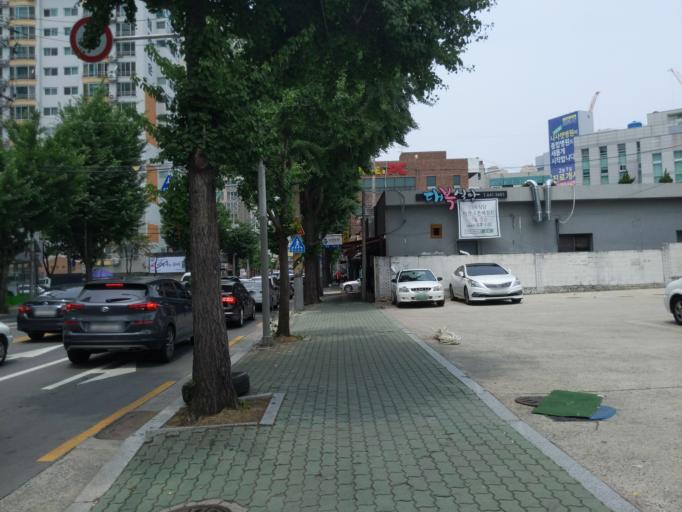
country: KR
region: Daegu
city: Hwawon
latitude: 35.8126
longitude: 128.5251
